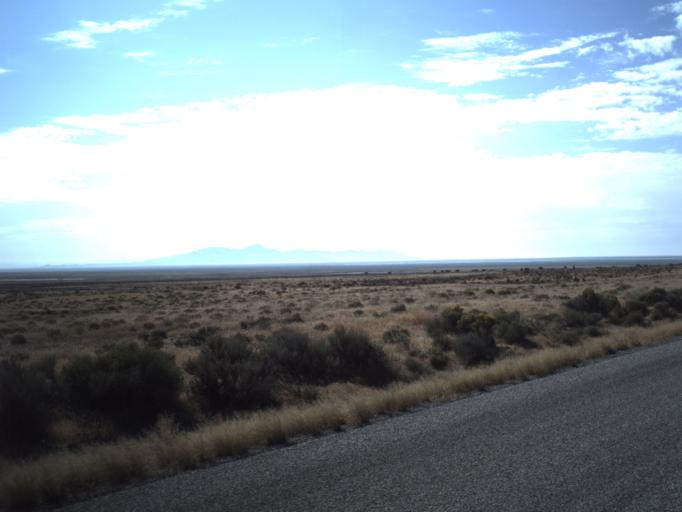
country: US
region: Utah
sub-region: Tooele County
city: Wendover
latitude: 41.5180
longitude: -113.5983
